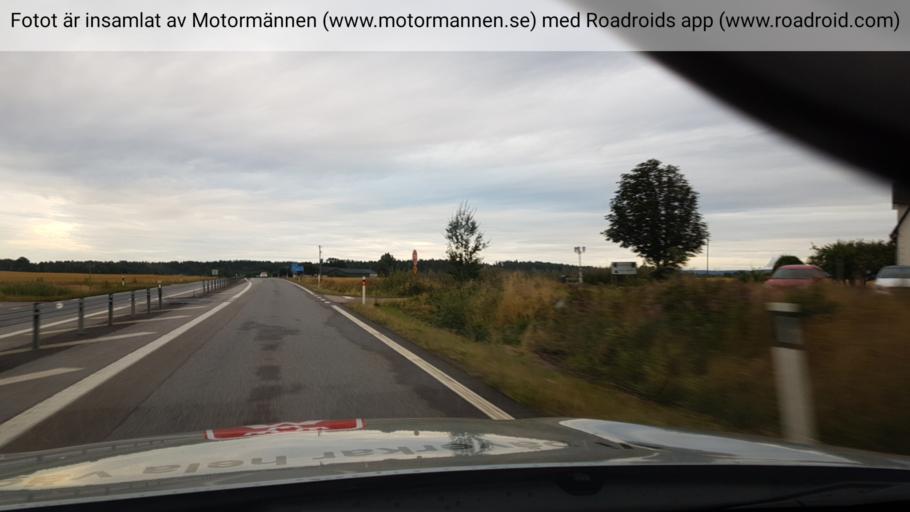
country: SE
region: Halland
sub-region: Laholms Kommun
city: Laholm
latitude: 56.4754
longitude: 13.0801
